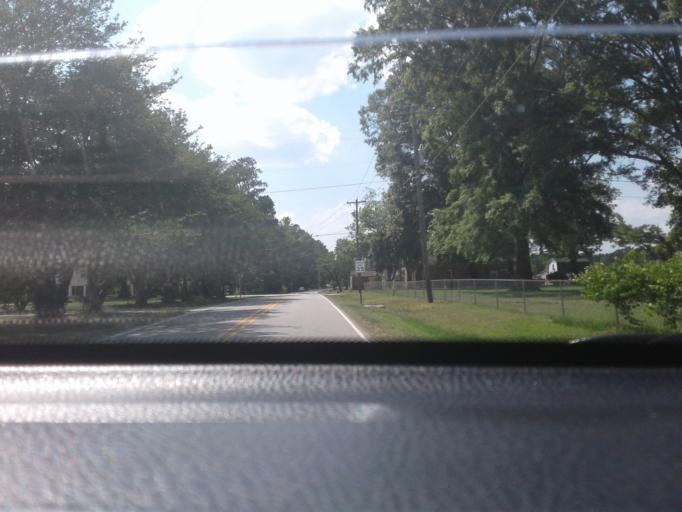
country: US
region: North Carolina
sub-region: Harnett County
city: Erwin
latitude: 35.2178
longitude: -78.6809
